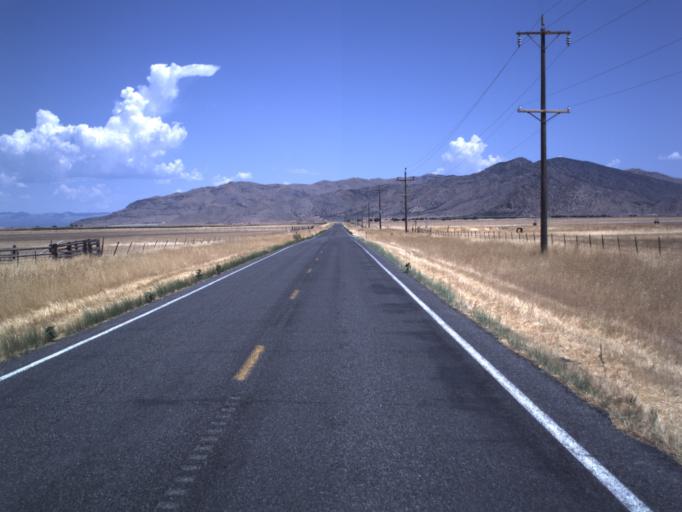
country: US
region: Utah
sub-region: Millard County
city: Delta
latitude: 39.4981
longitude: -112.2689
